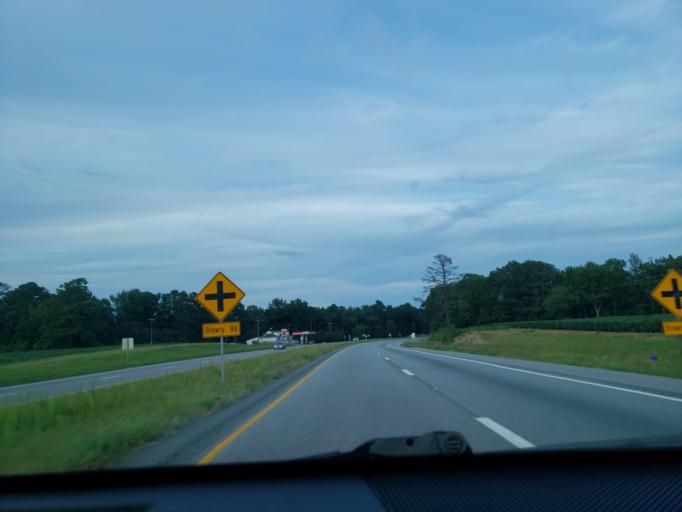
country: US
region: Virginia
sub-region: Sussex County
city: Sussex
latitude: 36.7064
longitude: -77.3071
